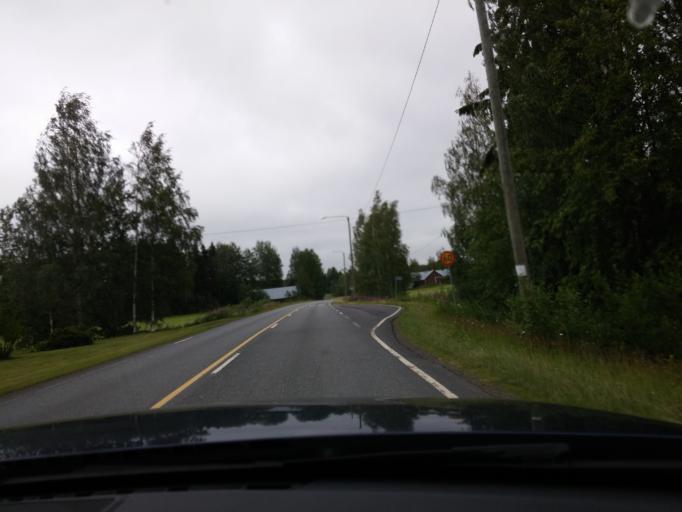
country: FI
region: Central Finland
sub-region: Joutsa
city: Joutsa
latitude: 61.8114
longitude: 25.9442
